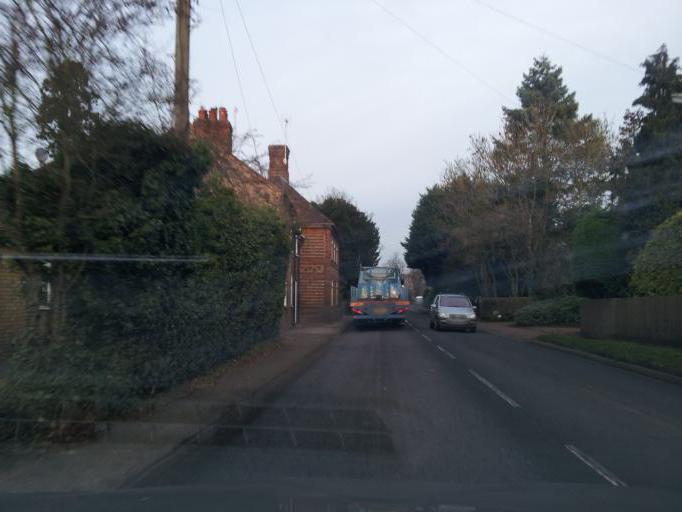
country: GB
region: England
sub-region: Buckinghamshire
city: Stewkley
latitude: 51.8922
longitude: -0.7208
